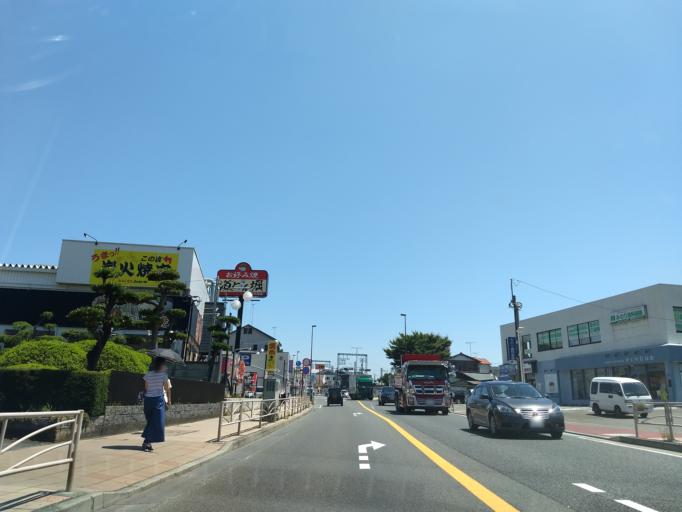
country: JP
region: Kanagawa
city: Atsugi
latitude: 35.4162
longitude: 139.3412
